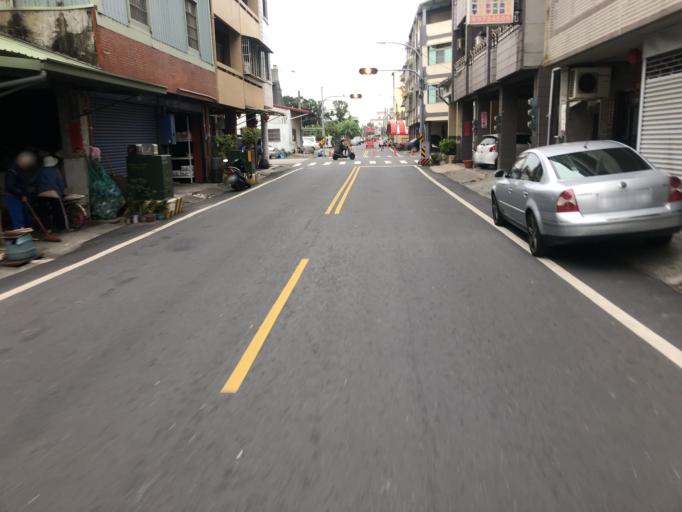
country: TW
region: Taiwan
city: Xinying
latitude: 23.1817
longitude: 120.2442
